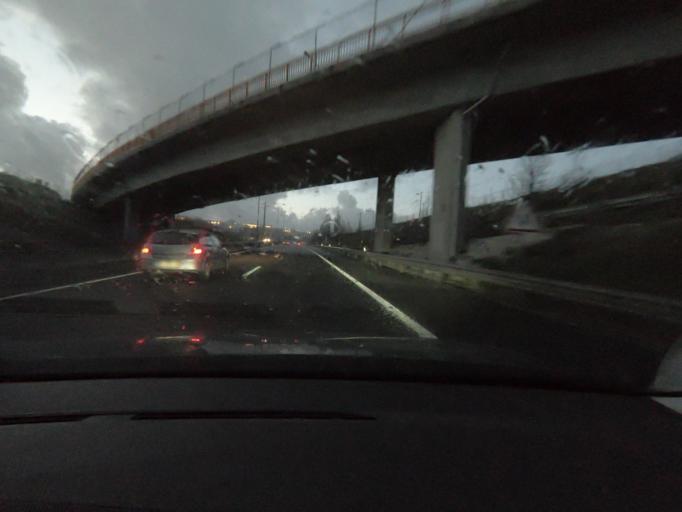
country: PT
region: Lisbon
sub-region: Oeiras
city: Porto Salvo
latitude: 38.7314
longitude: -9.2966
